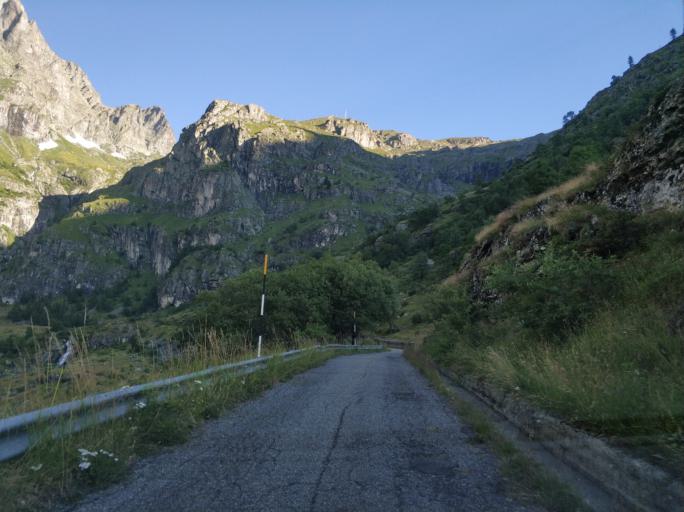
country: IT
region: Piedmont
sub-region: Provincia di Torino
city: Usseglio
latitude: 45.2462
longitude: 7.1790
